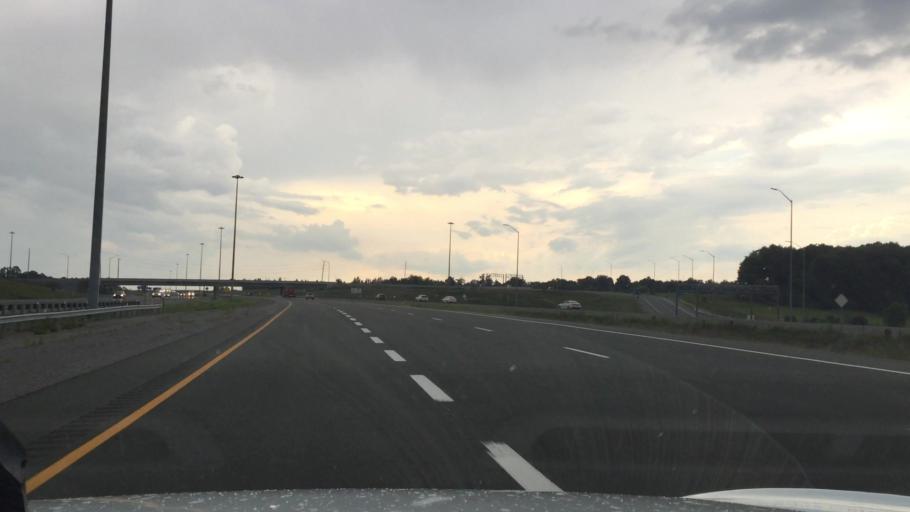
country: CA
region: Ontario
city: Ajax
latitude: 43.9508
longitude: -79.0148
